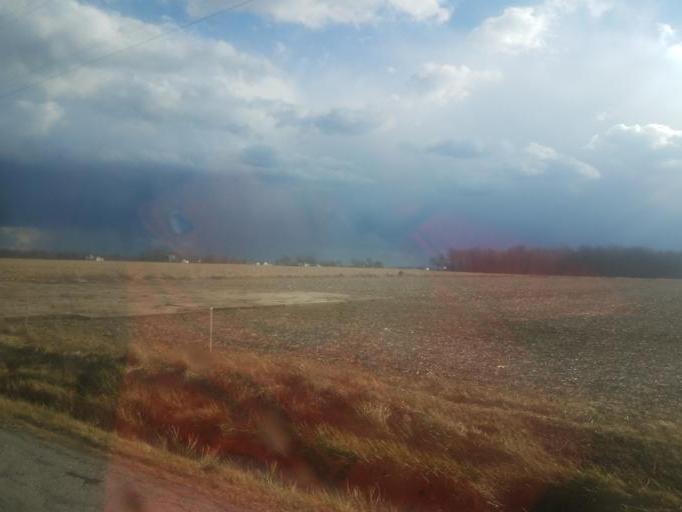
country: US
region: Ohio
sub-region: Marion County
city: Prospect
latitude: 40.4727
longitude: -83.1313
